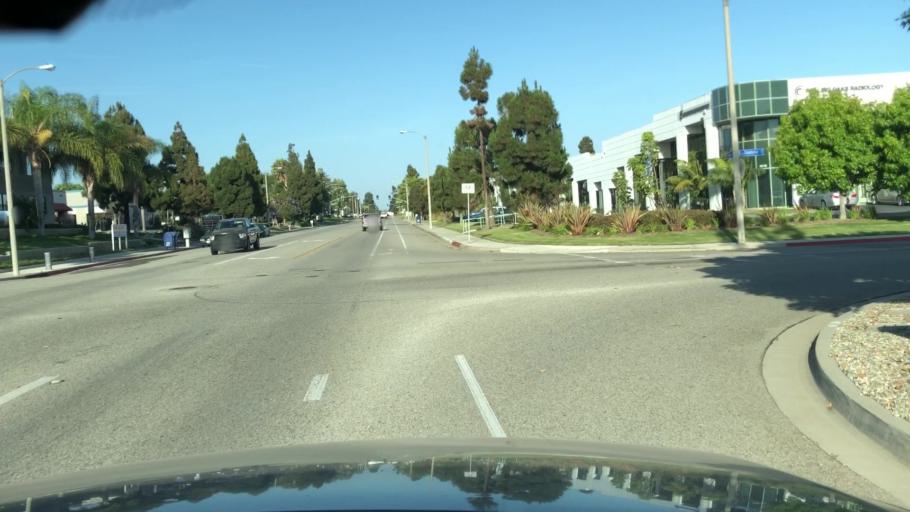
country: US
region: California
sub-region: Ventura County
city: Ventura
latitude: 34.2572
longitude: -119.2327
